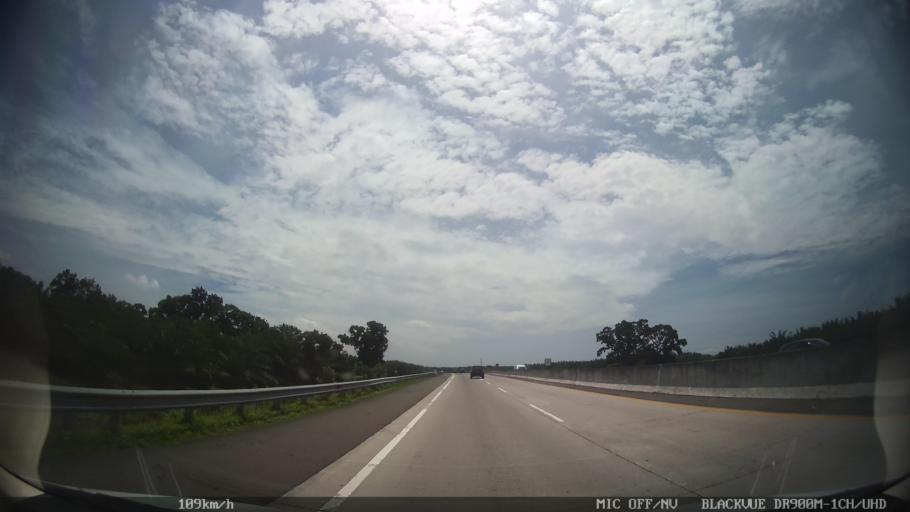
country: ID
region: North Sumatra
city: Perbaungan
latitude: 3.5323
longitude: 98.8740
